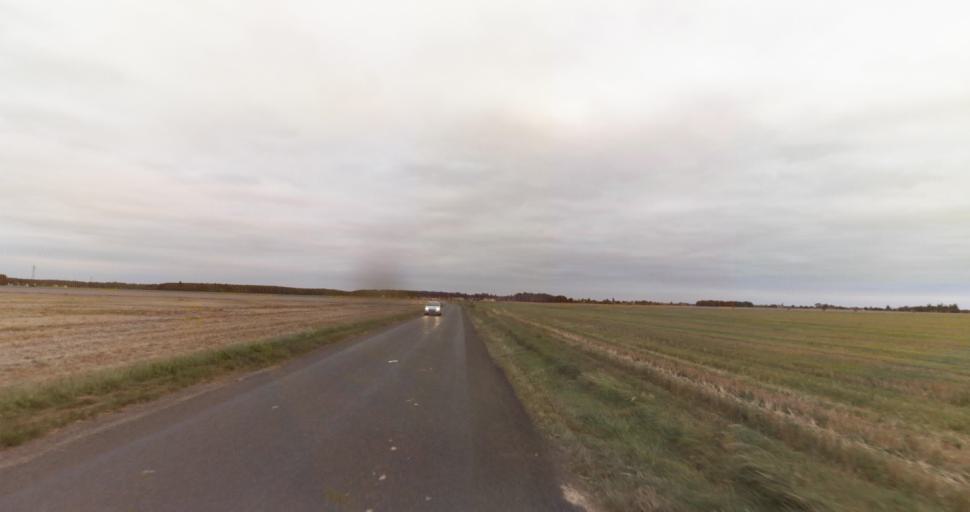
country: FR
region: Centre
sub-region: Departement d'Eure-et-Loir
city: Vert-en-Drouais
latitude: 48.7842
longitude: 1.2928
